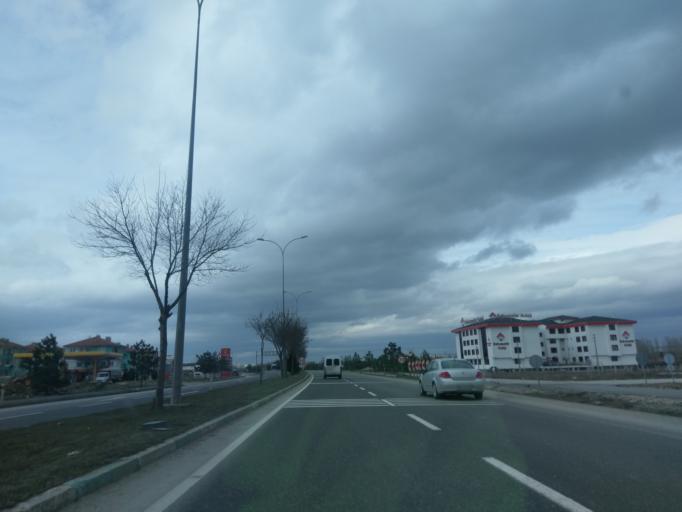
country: TR
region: Kuetahya
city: Kutahya
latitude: 39.4082
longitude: 30.0248
